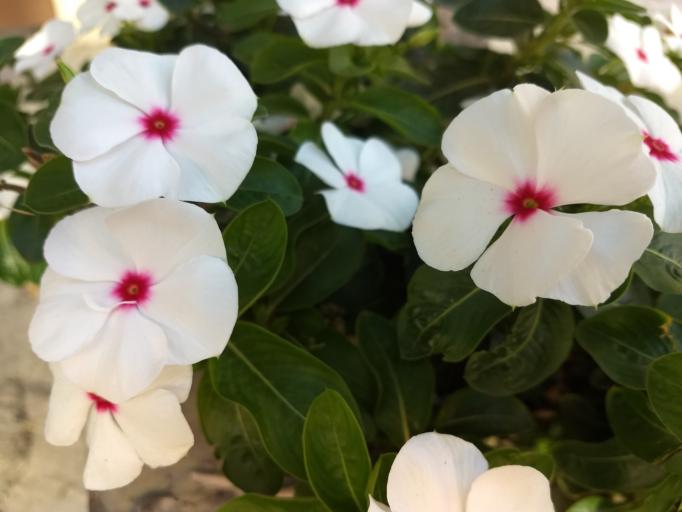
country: MX
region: Mexico City
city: Gustavo A. Madero
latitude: 19.4672
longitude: -99.1193
